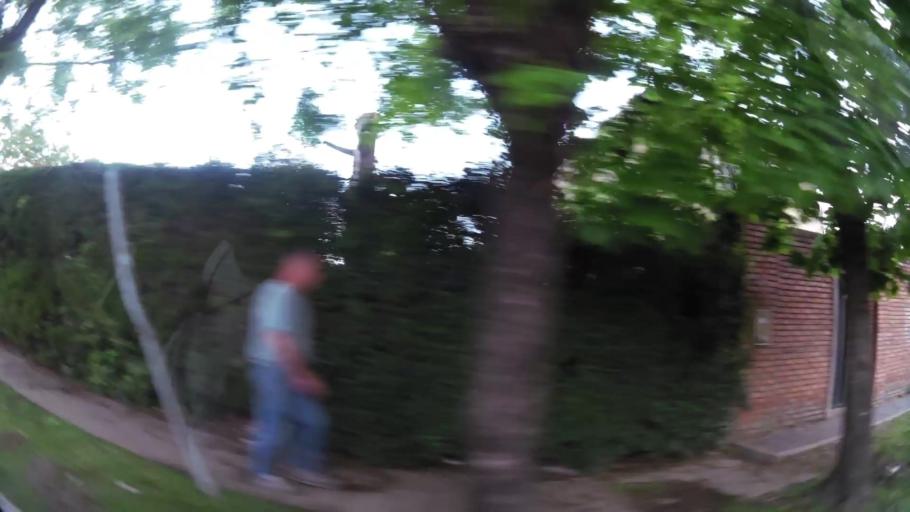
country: AR
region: Buenos Aires
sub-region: Partido de Quilmes
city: Quilmes
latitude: -34.7771
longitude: -58.2114
